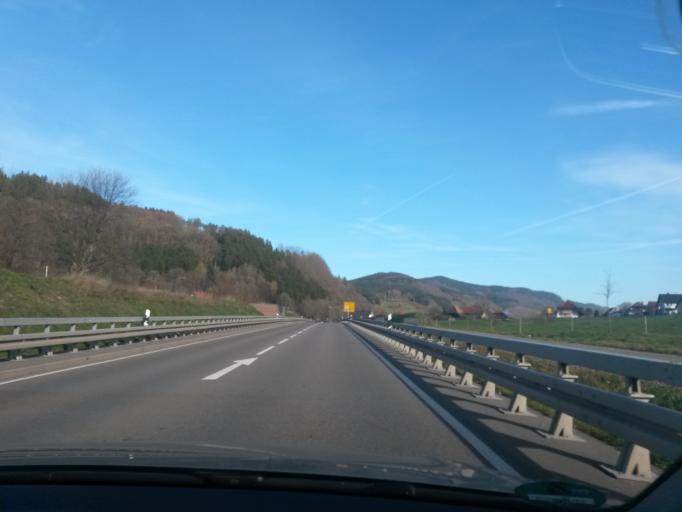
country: DE
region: Baden-Wuerttemberg
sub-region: Freiburg Region
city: Elzach
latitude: 48.1780
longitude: 8.0789
